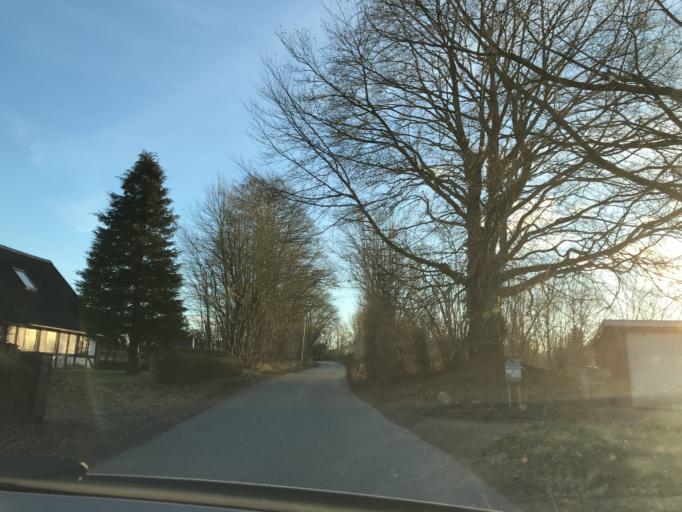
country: DK
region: South Denmark
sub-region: Middelfart Kommune
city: Brenderup
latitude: 55.4901
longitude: 9.9786
